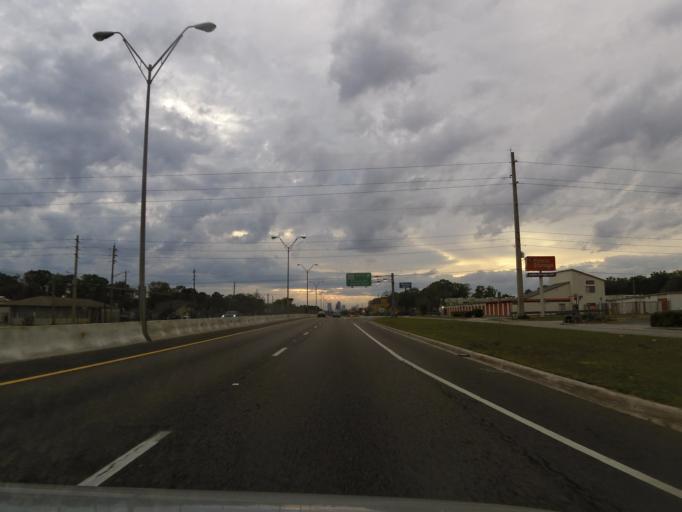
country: US
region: Florida
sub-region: Duval County
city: Jacksonville
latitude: 30.3271
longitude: -81.5908
